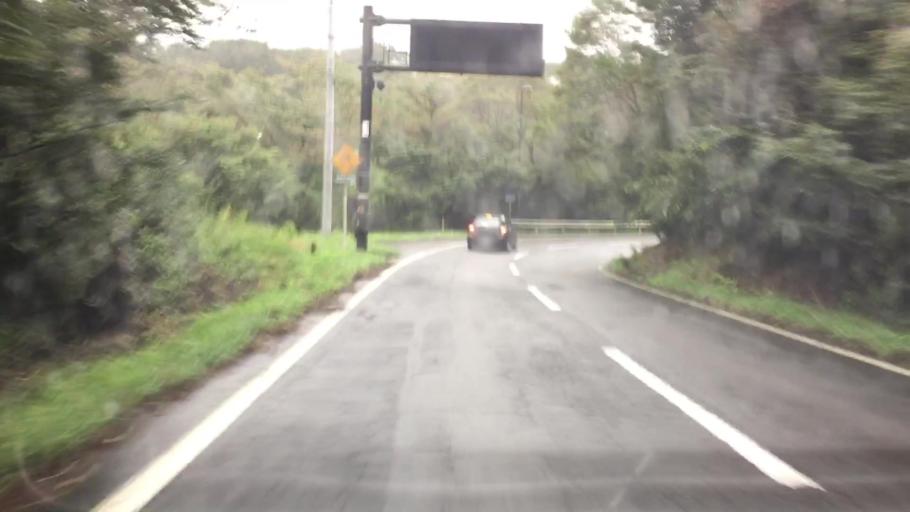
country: JP
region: Yamanashi
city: Fujikawaguchiko
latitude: 35.3940
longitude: 138.6086
